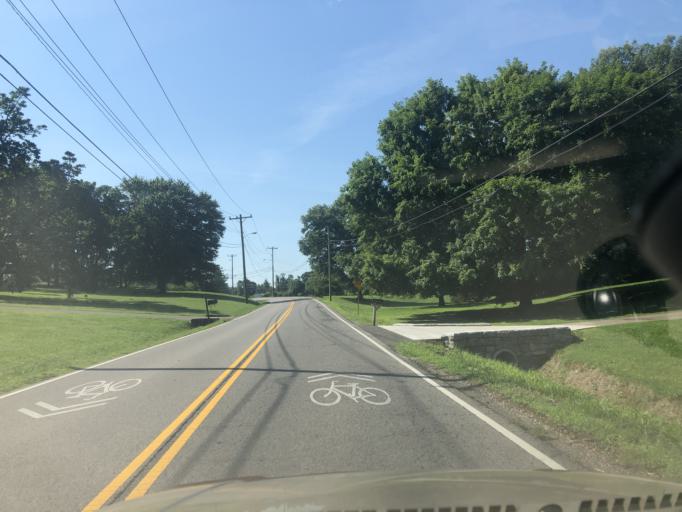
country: US
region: Tennessee
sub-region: Davidson County
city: Lakewood
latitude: 36.2306
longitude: -86.6945
